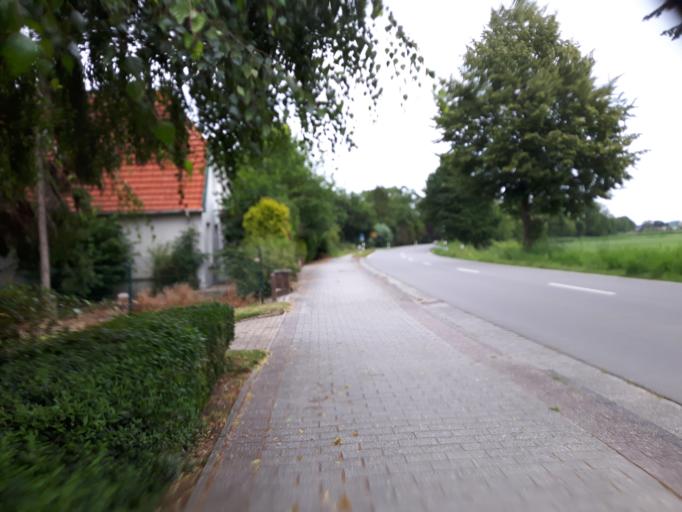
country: DE
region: Lower Saxony
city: Varel
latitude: 53.3872
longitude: 8.2419
